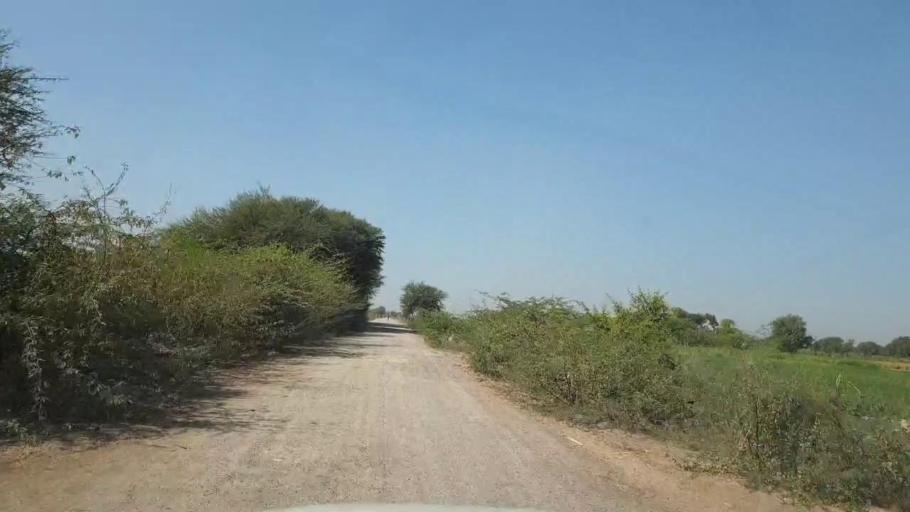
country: PK
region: Sindh
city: Kunri
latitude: 25.1282
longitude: 69.5306
